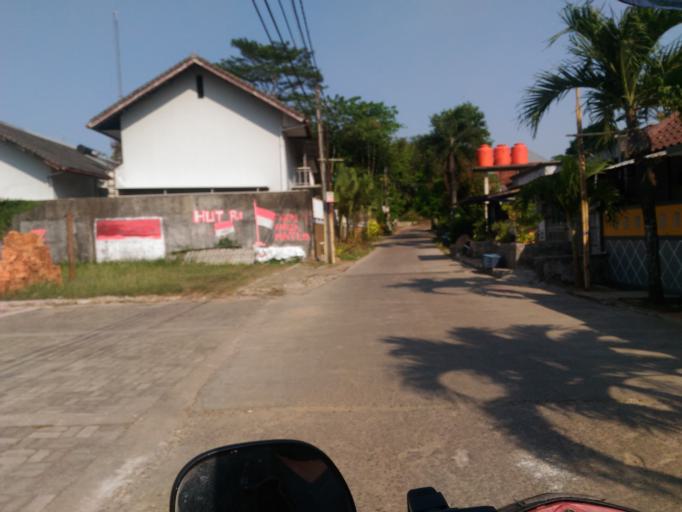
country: ID
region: West Java
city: Depok
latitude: -6.3430
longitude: 106.8393
